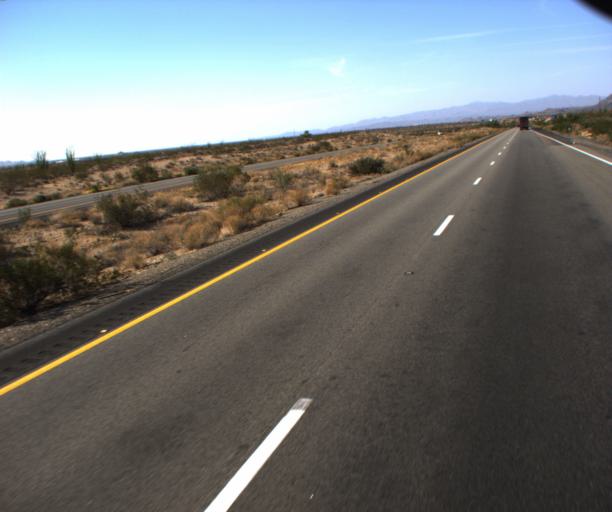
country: US
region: Arizona
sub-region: Mohave County
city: Kingman
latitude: 34.9086
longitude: -114.1538
